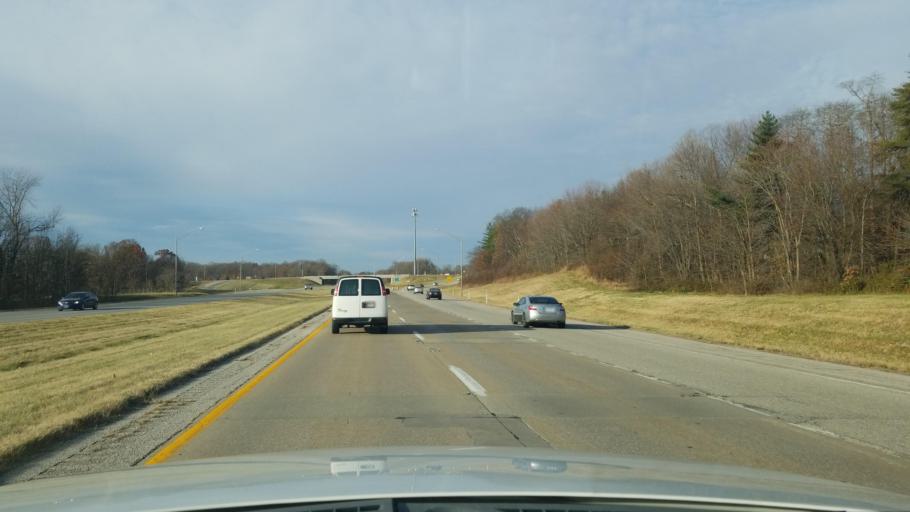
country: US
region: Indiana
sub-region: Vanderburgh County
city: Evansville
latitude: 37.9684
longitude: -87.6709
